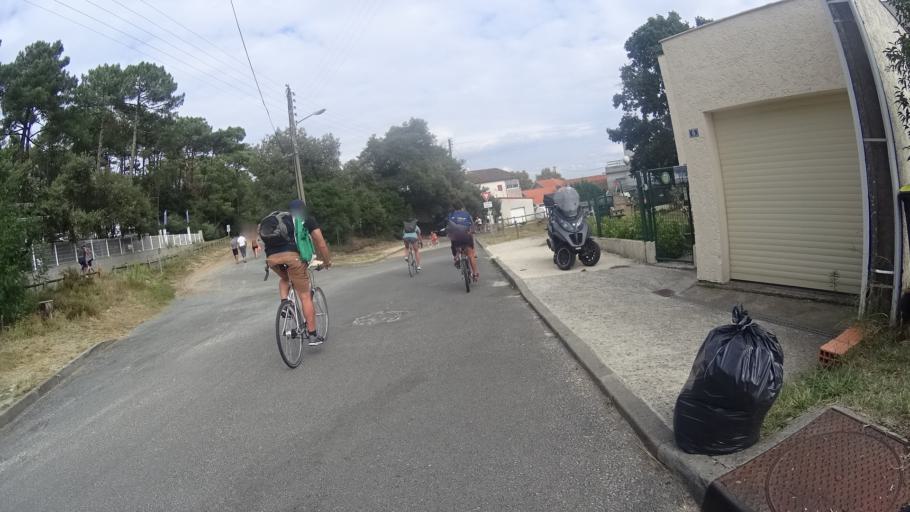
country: FR
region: Aquitaine
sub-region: Departement de la Gironde
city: Lacanau
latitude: 45.0031
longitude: -1.1353
